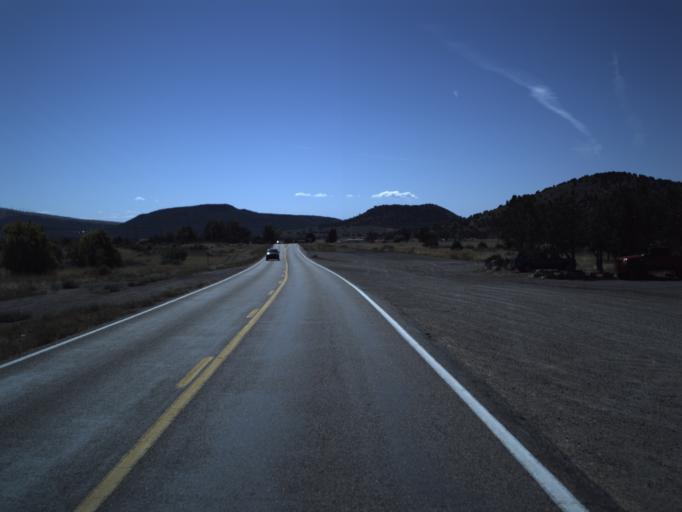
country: US
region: Utah
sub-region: Washington County
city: Enterprise
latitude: 37.4211
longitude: -113.6313
